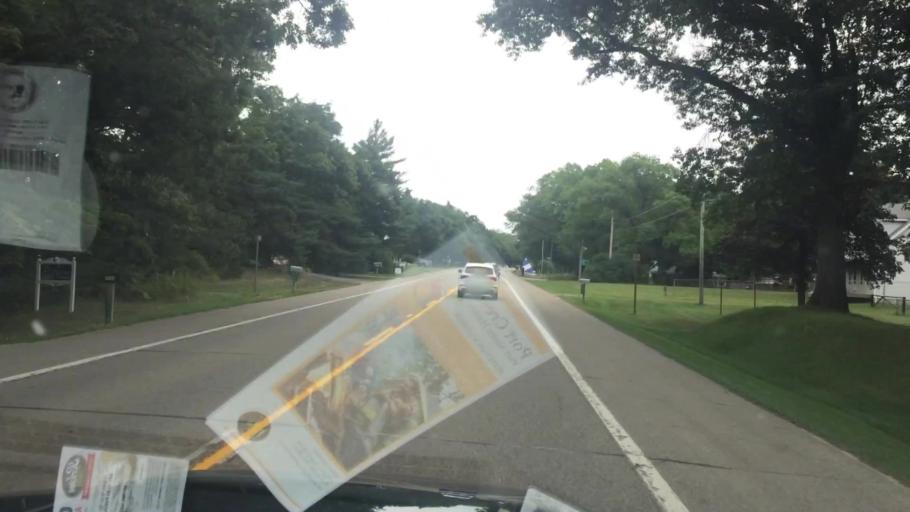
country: US
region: Michigan
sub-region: Huron County
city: Pigeon
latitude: 43.9816
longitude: -83.2012
